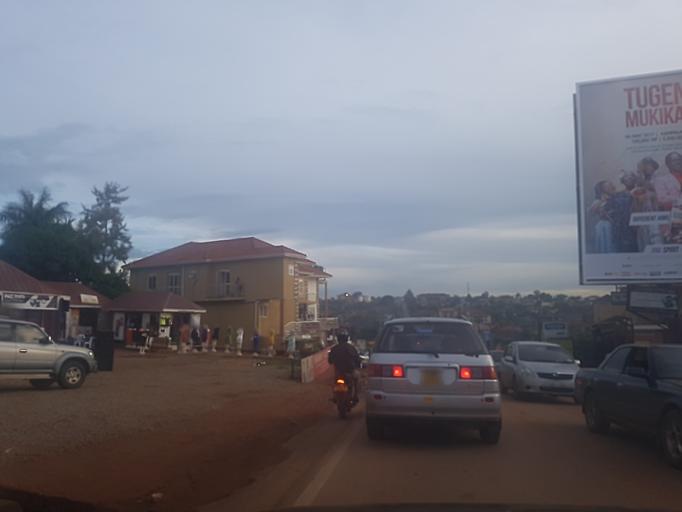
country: UG
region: Central Region
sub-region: Wakiso District
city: Kireka
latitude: 0.3762
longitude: 32.6442
